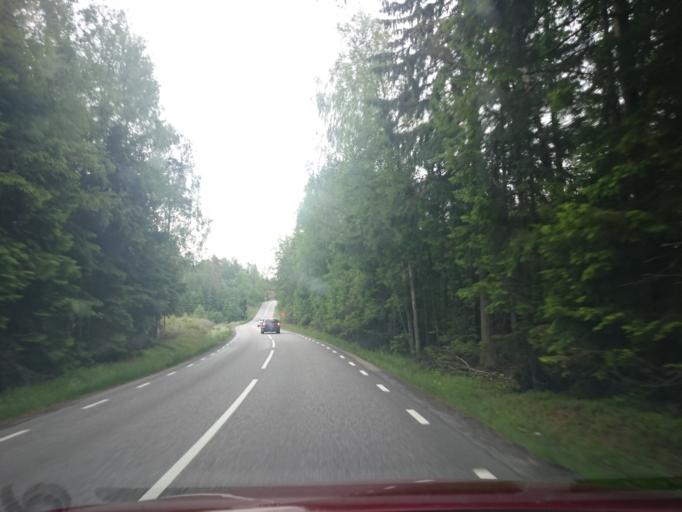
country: SE
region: Vaestra Goetaland
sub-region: Harryda Kommun
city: Hindas
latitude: 57.7012
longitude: 12.3506
